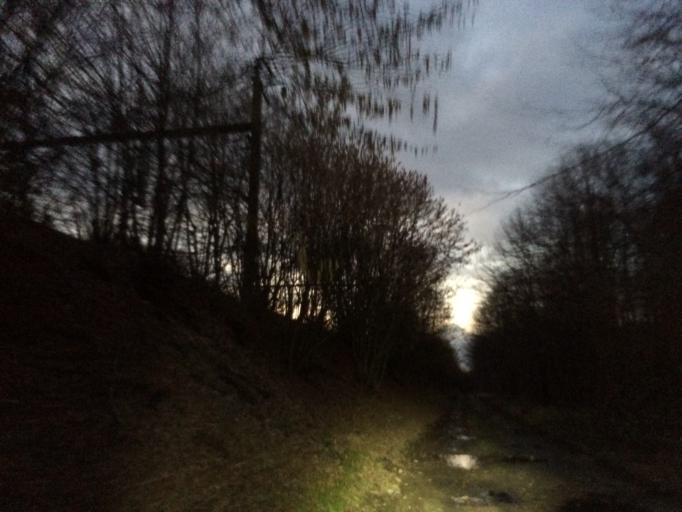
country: FR
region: Picardie
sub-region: Departement de l'Oise
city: Coye-la-Foret
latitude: 49.1425
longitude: 2.4868
